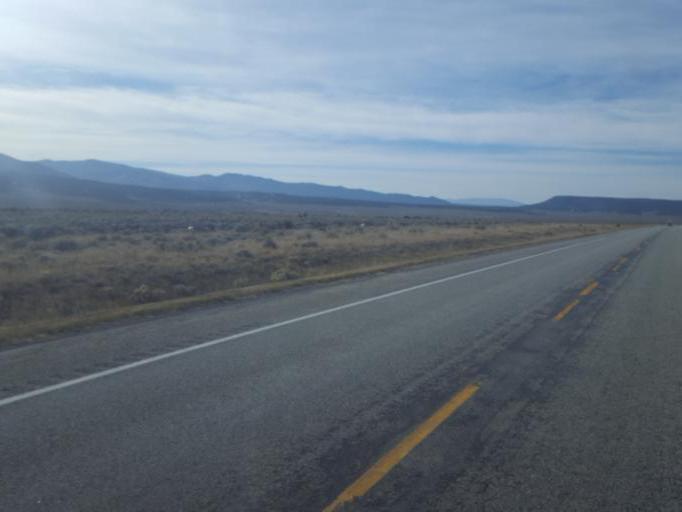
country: US
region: Colorado
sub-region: Costilla County
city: San Luis
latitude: 37.4697
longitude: -105.3518
